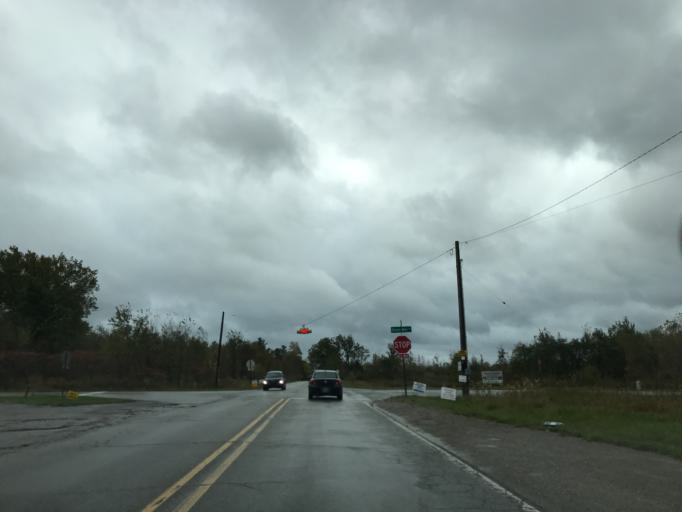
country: US
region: Michigan
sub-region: Oakland County
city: South Lyon
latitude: 42.4143
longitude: -83.6465
